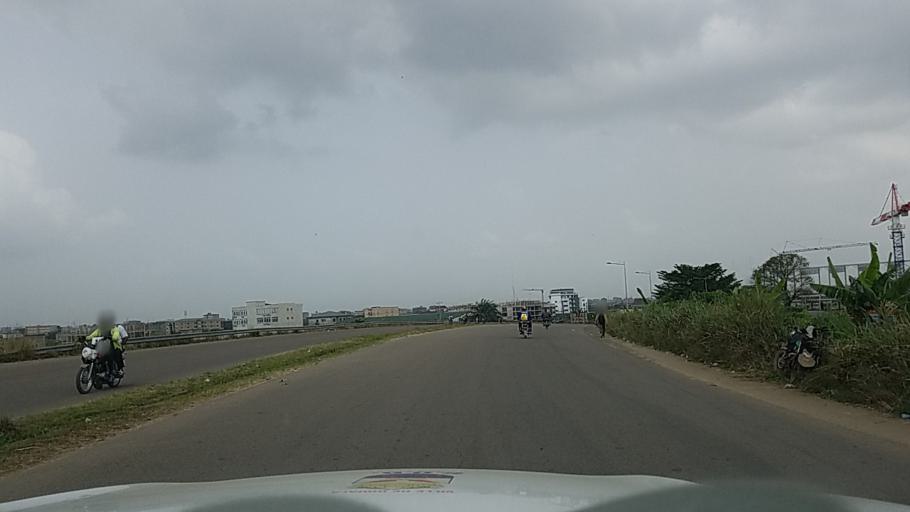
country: CM
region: Littoral
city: Douala
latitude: 4.0206
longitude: 9.7184
